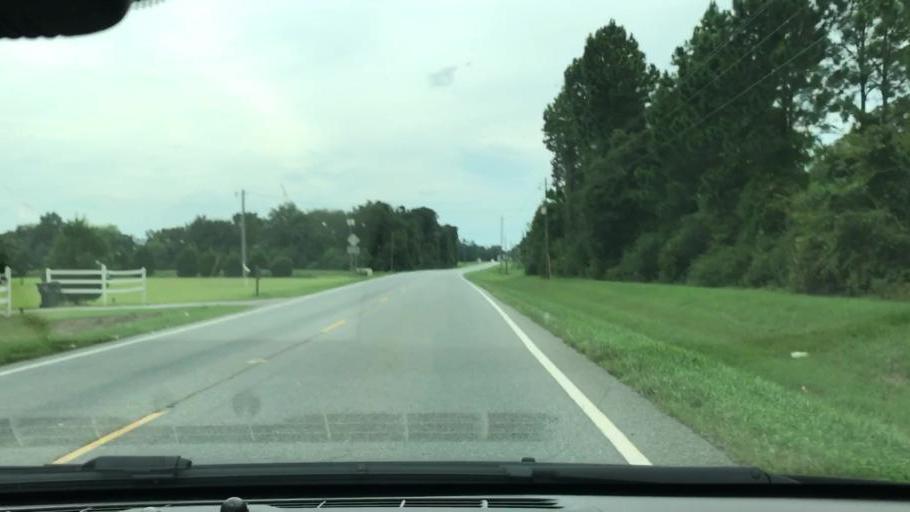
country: US
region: Georgia
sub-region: Early County
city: Blakely
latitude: 31.3817
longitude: -84.9574
